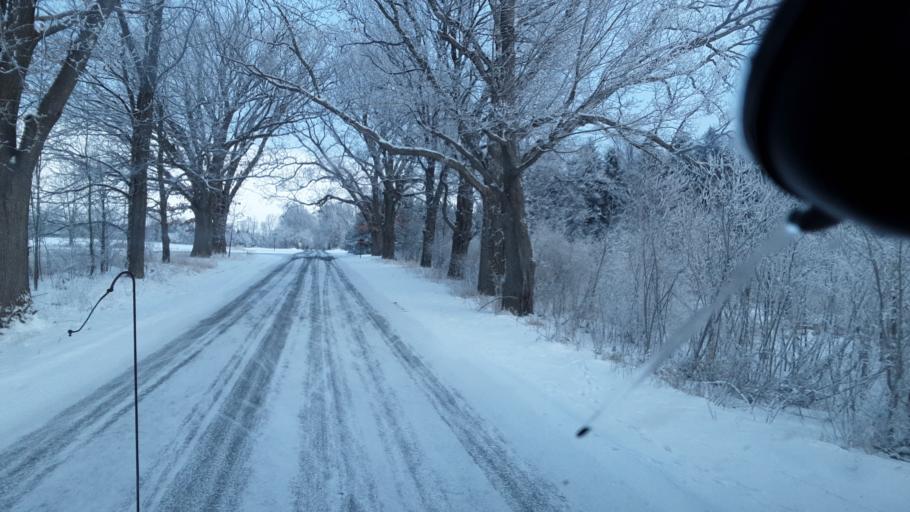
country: US
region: Michigan
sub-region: Ingham County
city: Leslie
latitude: 42.4357
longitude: -84.4970
